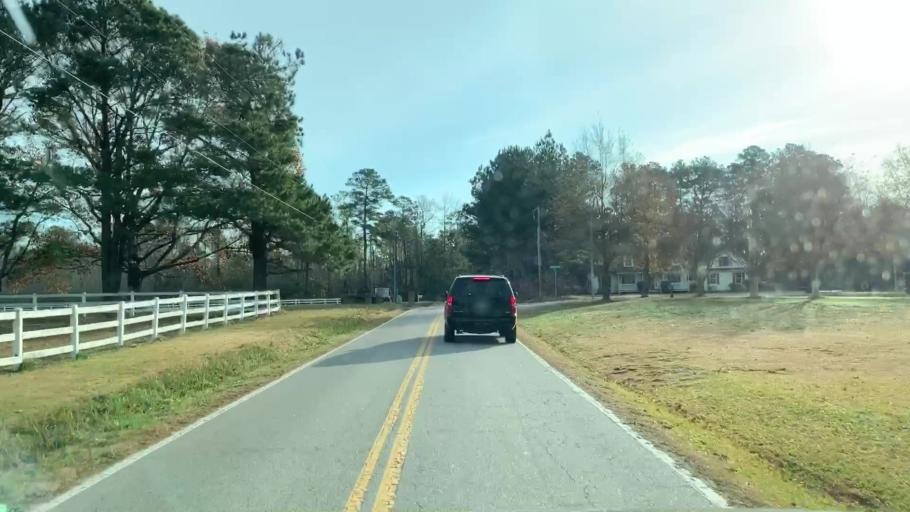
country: US
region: Virginia
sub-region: City of Virginia Beach
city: Virginia Beach
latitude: 36.6858
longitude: -75.9956
